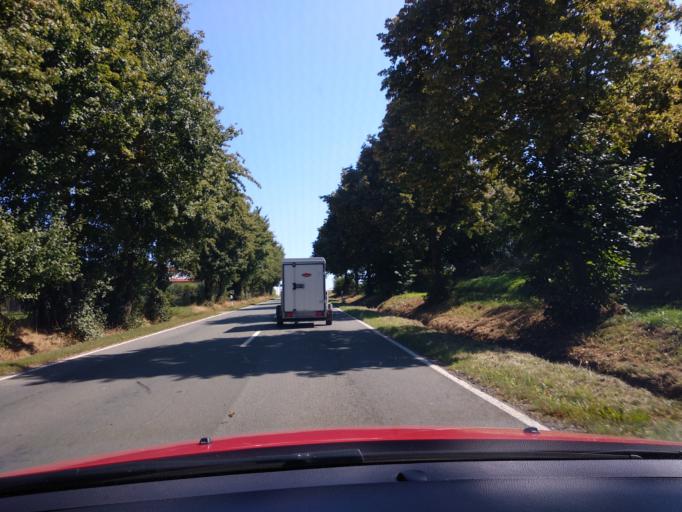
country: DE
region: North Rhine-Westphalia
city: Brakel
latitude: 51.6529
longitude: 9.1285
